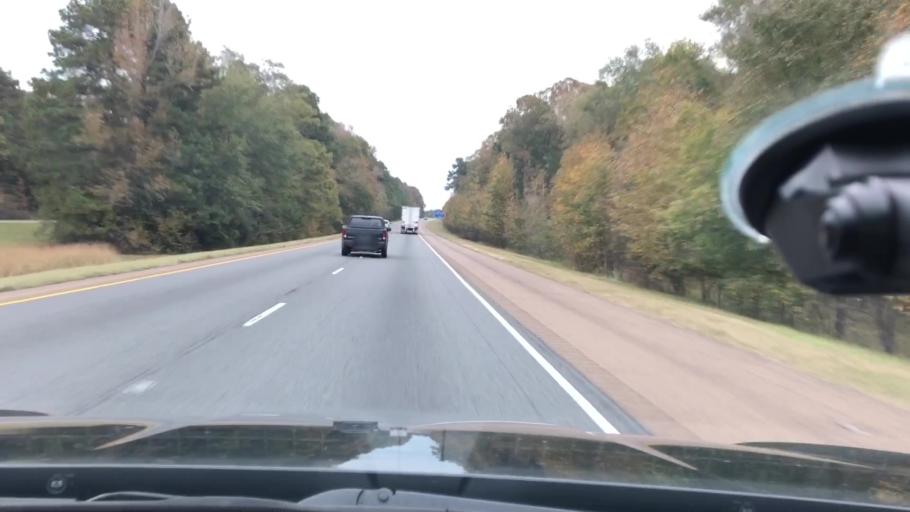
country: US
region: Arkansas
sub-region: Clark County
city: Gurdon
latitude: 33.9168
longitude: -93.2784
